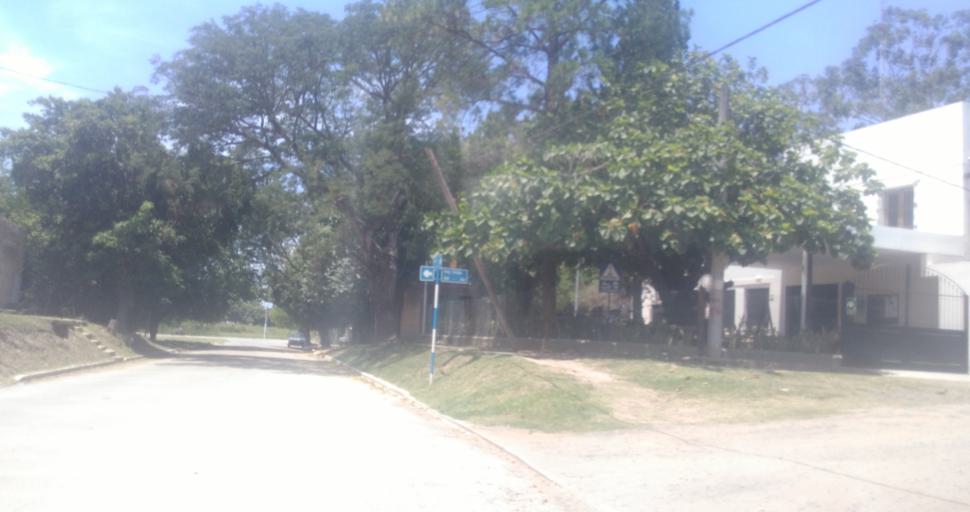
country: AR
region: Chaco
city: Fontana
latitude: -27.4151
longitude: -59.0289
